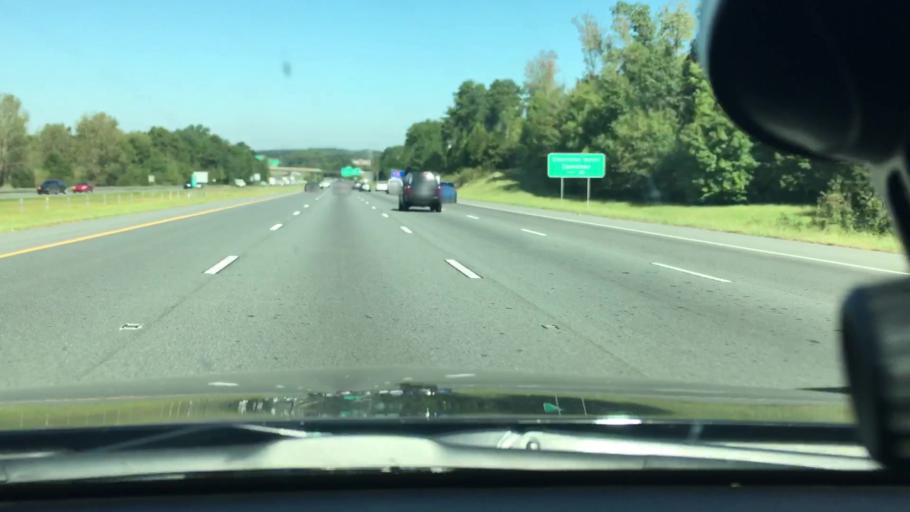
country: US
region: North Carolina
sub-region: Cabarrus County
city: Harrisburg
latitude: 35.3241
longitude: -80.7149
